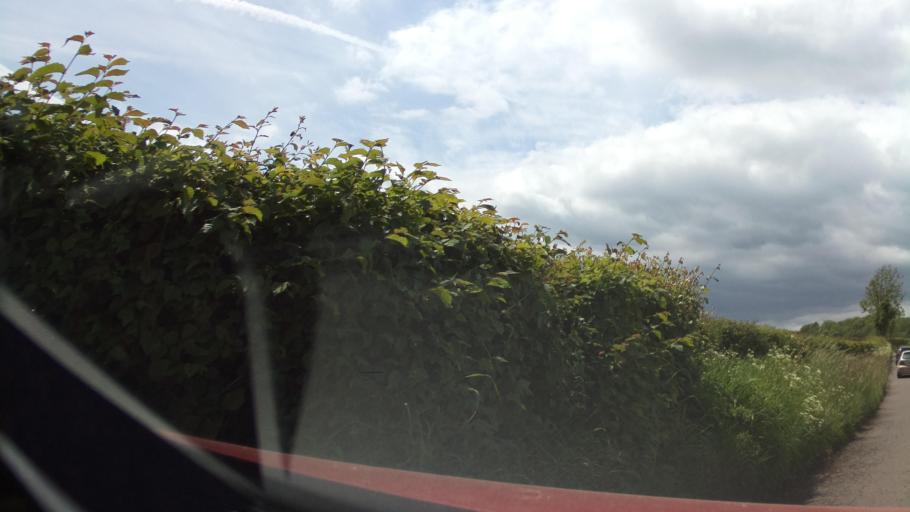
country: GB
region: England
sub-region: Herefordshire
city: Llanrothal
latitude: 51.8472
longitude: -2.7897
